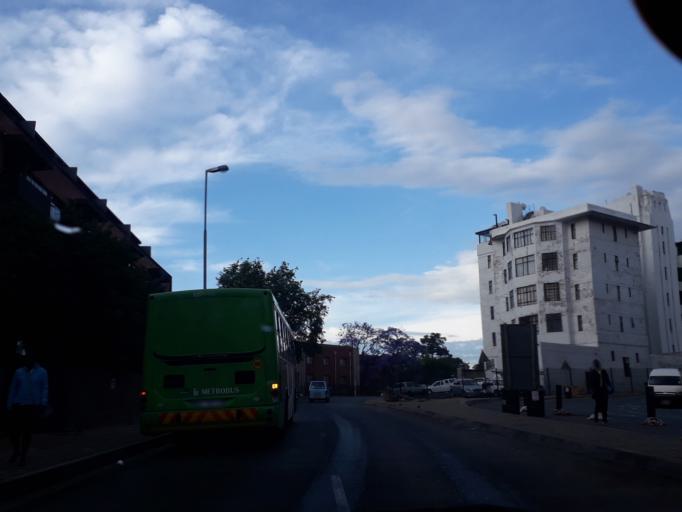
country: ZA
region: Gauteng
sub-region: City of Johannesburg Metropolitan Municipality
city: Johannesburg
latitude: -26.1829
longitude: 28.0480
